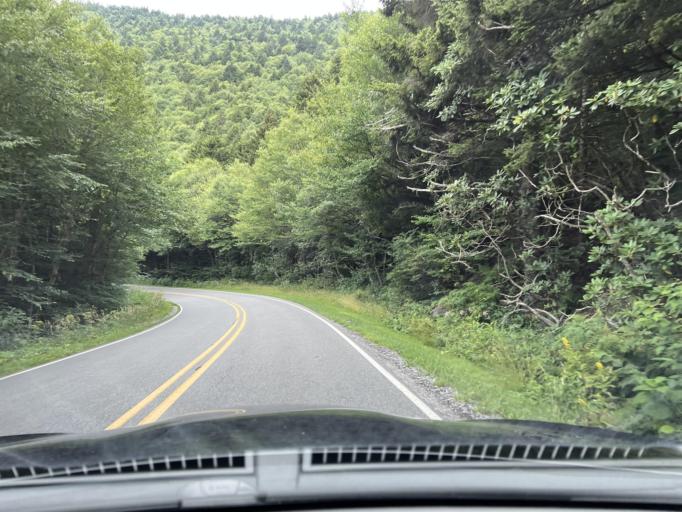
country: US
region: North Carolina
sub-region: Buncombe County
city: Black Mountain
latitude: 35.7381
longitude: -82.2803
